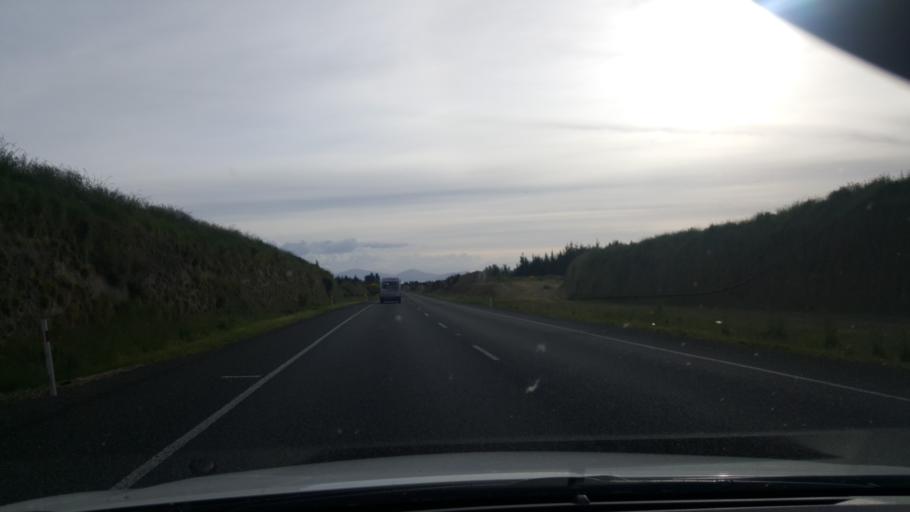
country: NZ
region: Waikato
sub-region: Taupo District
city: Taupo
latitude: -38.7247
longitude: 176.0955
